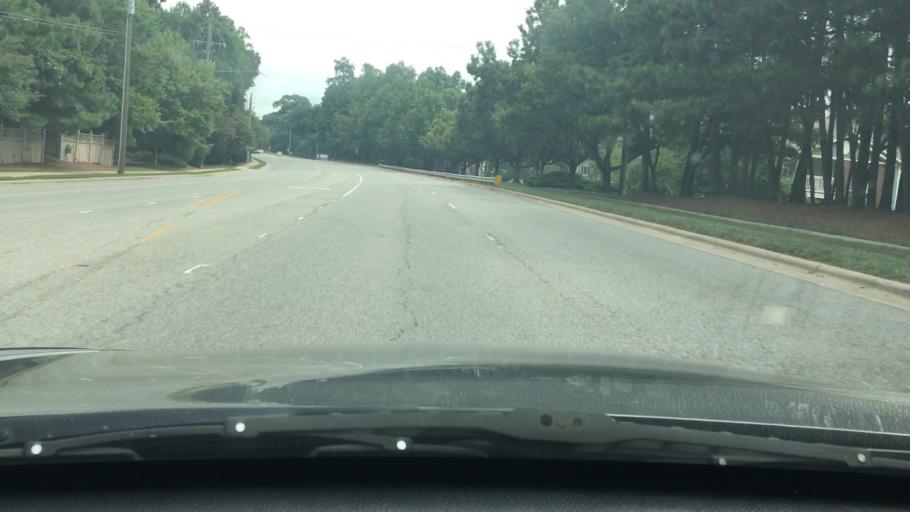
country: US
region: North Carolina
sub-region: Wake County
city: West Raleigh
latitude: 35.8364
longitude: -78.7132
